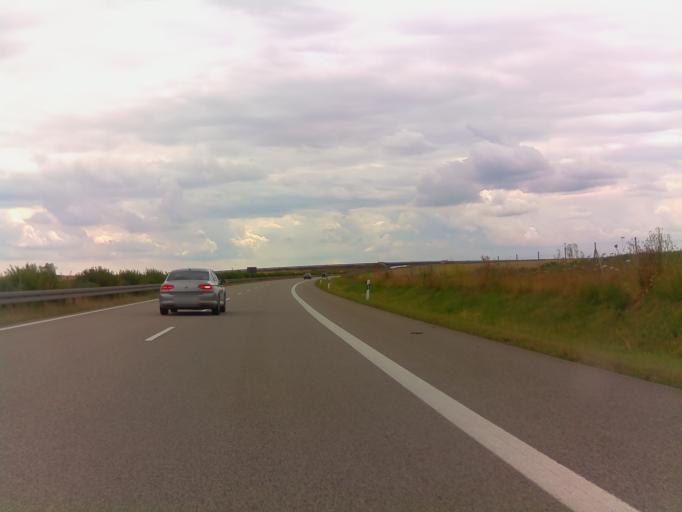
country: DE
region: Thuringia
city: Wolfershausen
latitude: 50.4340
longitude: 10.4283
